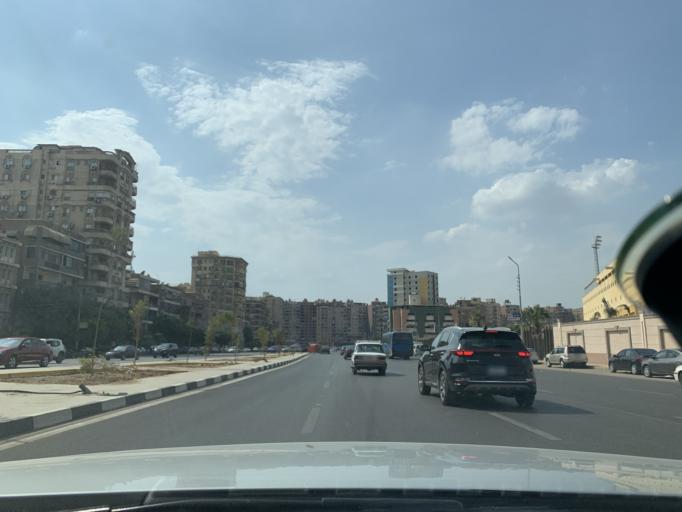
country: EG
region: Muhafazat al Qalyubiyah
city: Al Khankah
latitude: 30.1156
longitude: 31.3429
